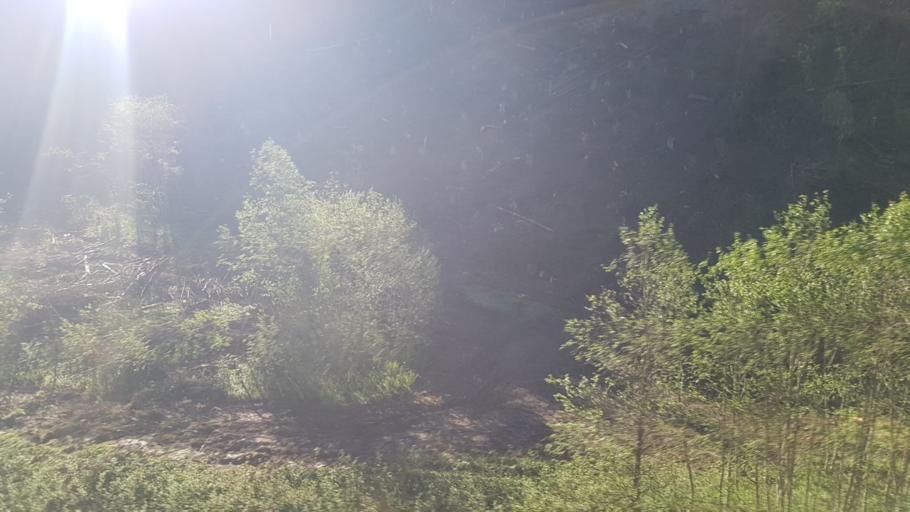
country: NO
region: Sor-Trondelag
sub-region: Melhus
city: Melhus
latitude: 63.2427
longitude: 10.2778
